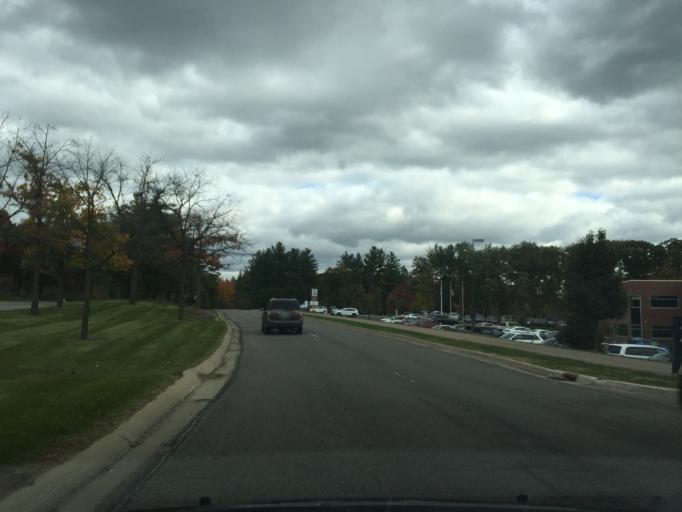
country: US
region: Michigan
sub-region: Oakland County
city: Auburn Hills
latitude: 42.6646
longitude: -83.2256
